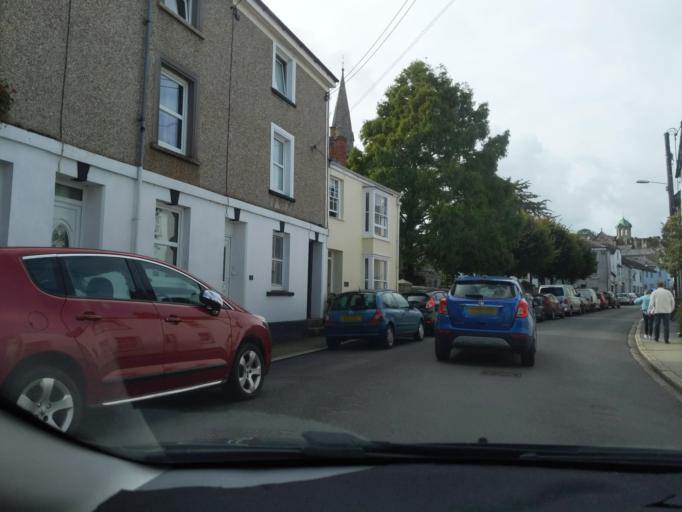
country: GB
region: England
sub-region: Cornwall
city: Lostwithiel
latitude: 50.4076
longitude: -4.6682
